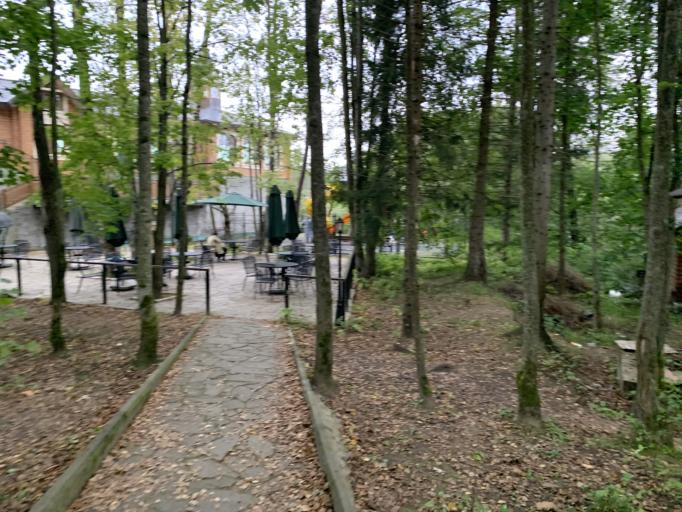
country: RU
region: Moskovskaya
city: Zvenigorod
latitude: 55.7352
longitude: 36.8115
